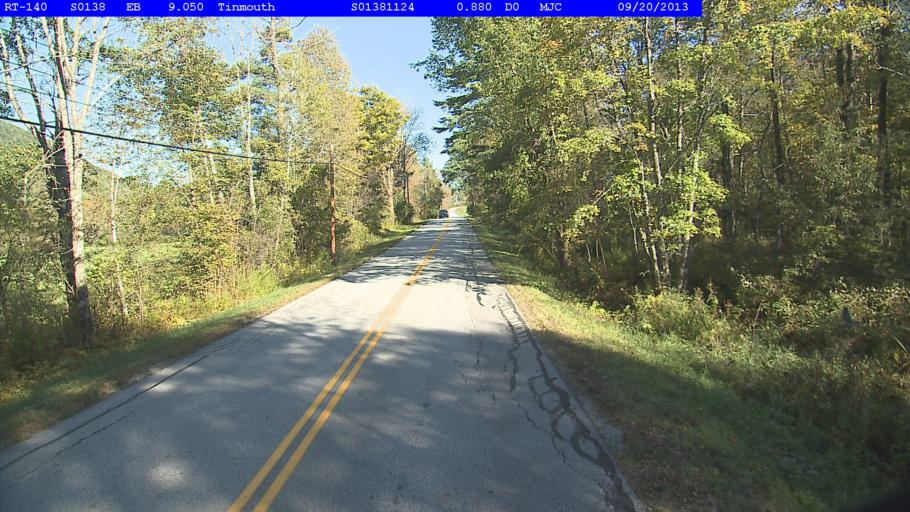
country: US
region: Vermont
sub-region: Rutland County
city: West Rutland
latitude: 43.4762
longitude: -73.0633
